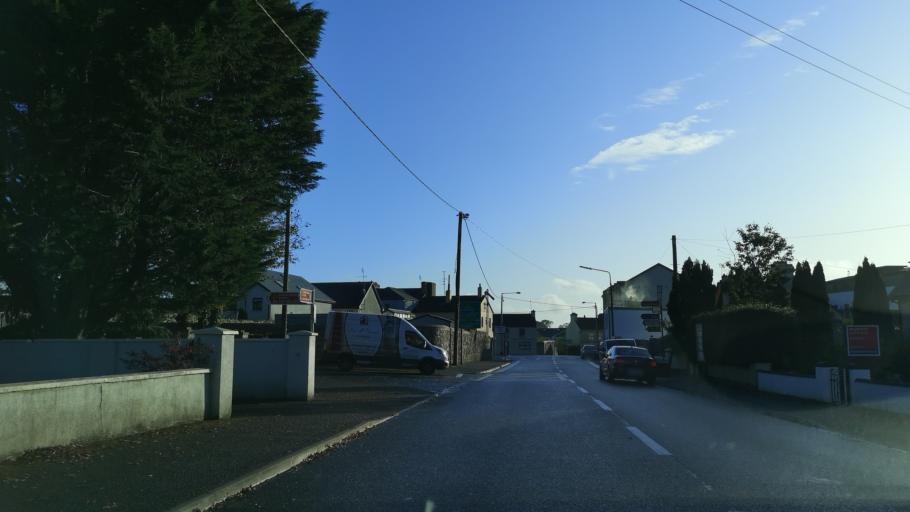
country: IE
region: Connaught
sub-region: Roscommon
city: Castlerea
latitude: 53.7706
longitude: -8.4945
